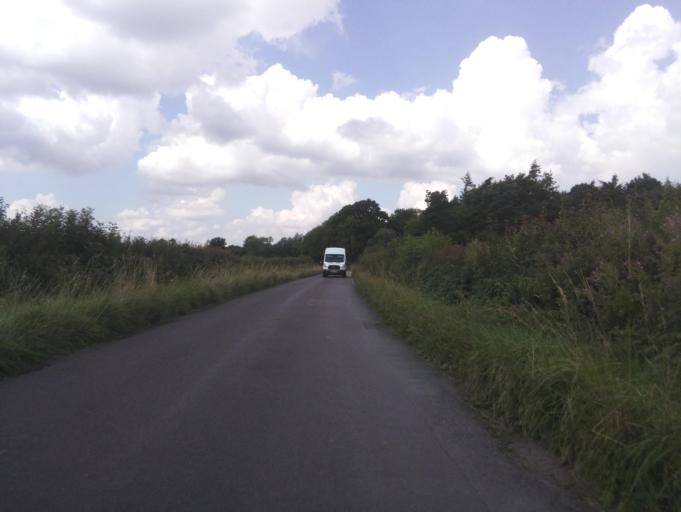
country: GB
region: England
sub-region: Wiltshire
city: Hankerton
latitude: 51.6332
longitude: -2.0603
